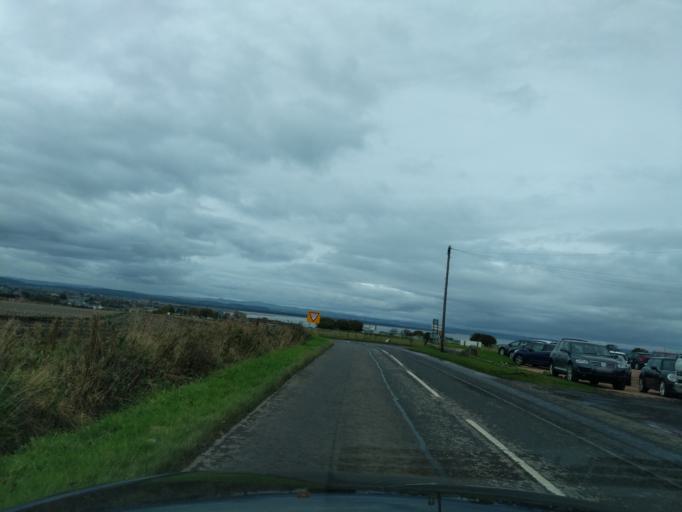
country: GB
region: Scotland
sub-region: Fife
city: Saint Andrews
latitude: 56.3262
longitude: -2.7706
